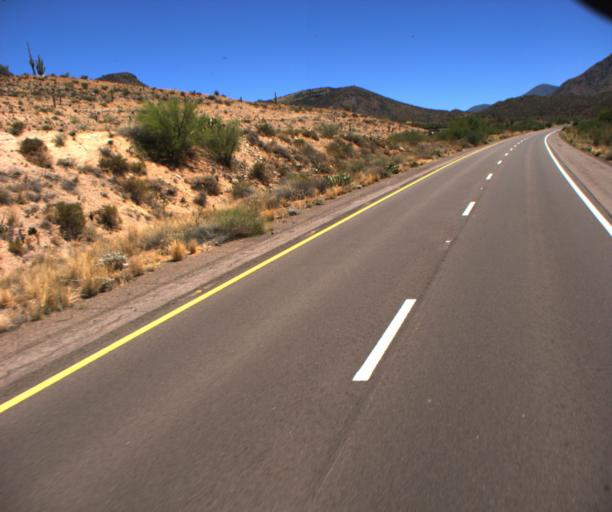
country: US
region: Arizona
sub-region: Gila County
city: Tonto Basin
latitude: 33.7992
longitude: -111.4906
